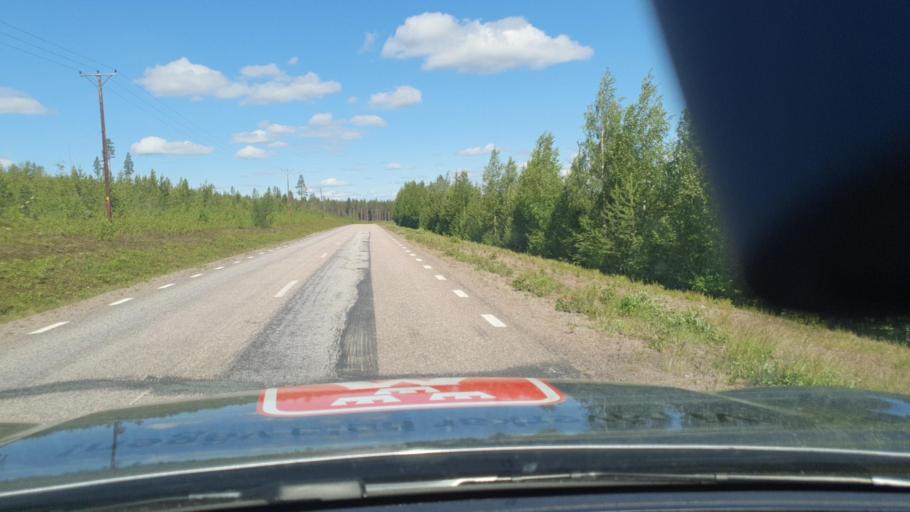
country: SE
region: Norrbotten
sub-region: Overkalix Kommun
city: OEverkalix
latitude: 67.0302
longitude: 22.5091
